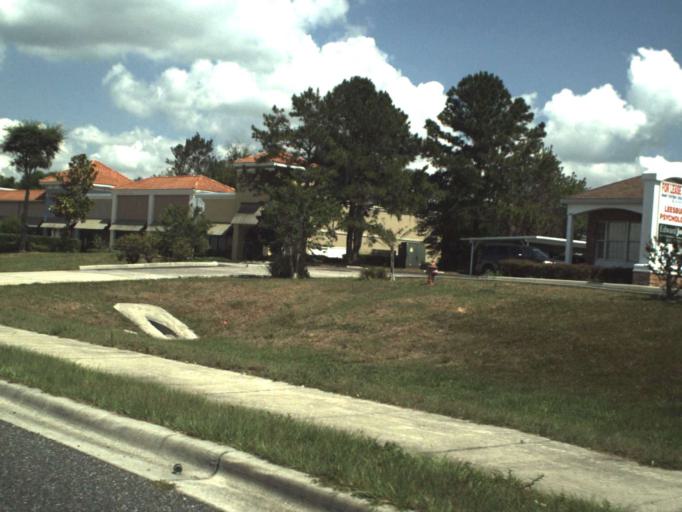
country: US
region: Florida
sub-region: Lake County
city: Silver Lake
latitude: 28.8321
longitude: -81.8152
